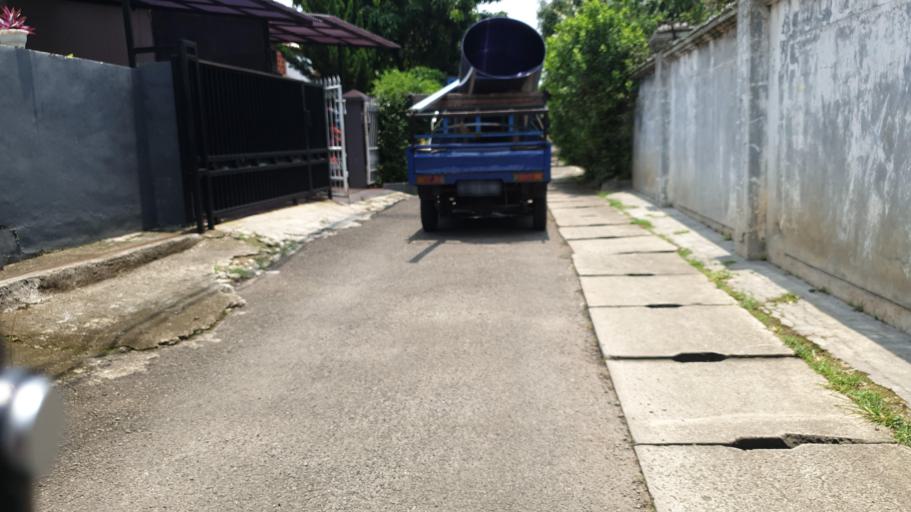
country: ID
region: West Java
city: Pamulang
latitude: -6.3013
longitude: 106.7776
